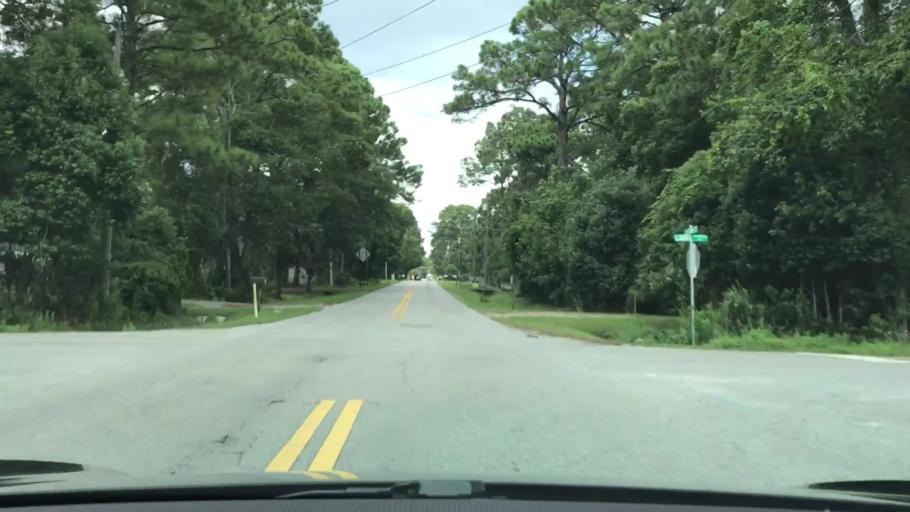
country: US
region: Florida
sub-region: Bay County
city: Panama City Beach
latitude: 30.1785
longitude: -85.7865
